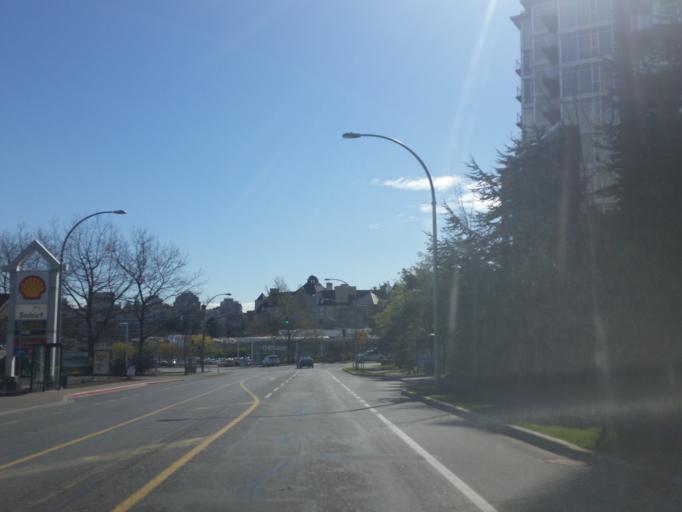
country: CA
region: British Columbia
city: Victoria
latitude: 48.4290
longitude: -123.3785
